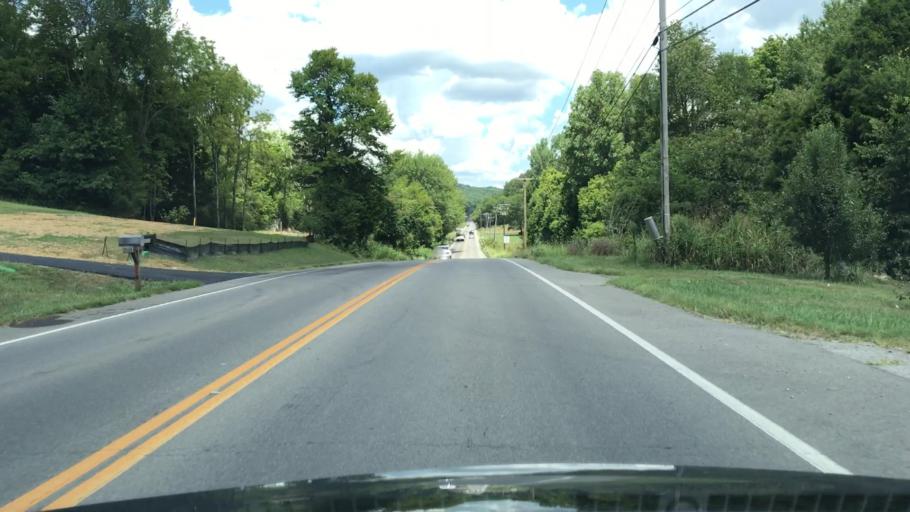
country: US
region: Tennessee
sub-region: Williamson County
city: Nolensville
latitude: 35.8821
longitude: -86.6621
